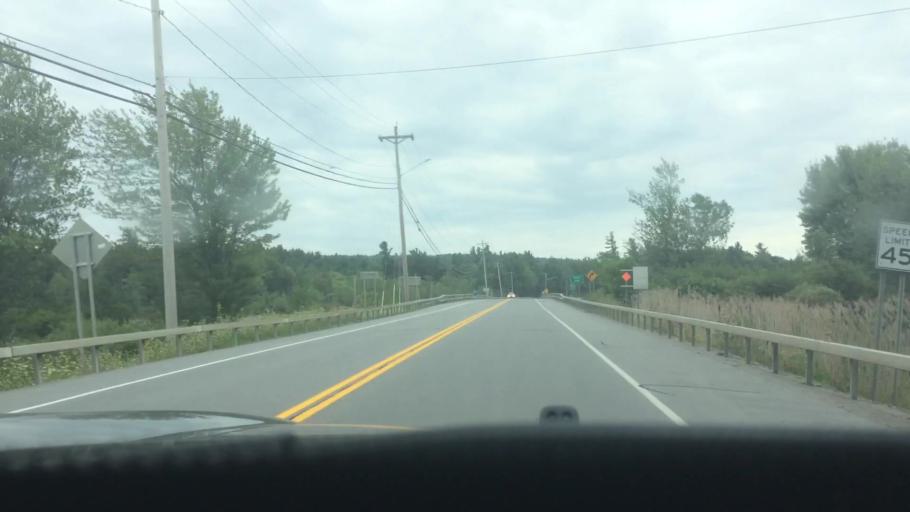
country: US
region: New York
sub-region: St. Lawrence County
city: Hannawa Falls
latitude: 44.5498
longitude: -74.9358
